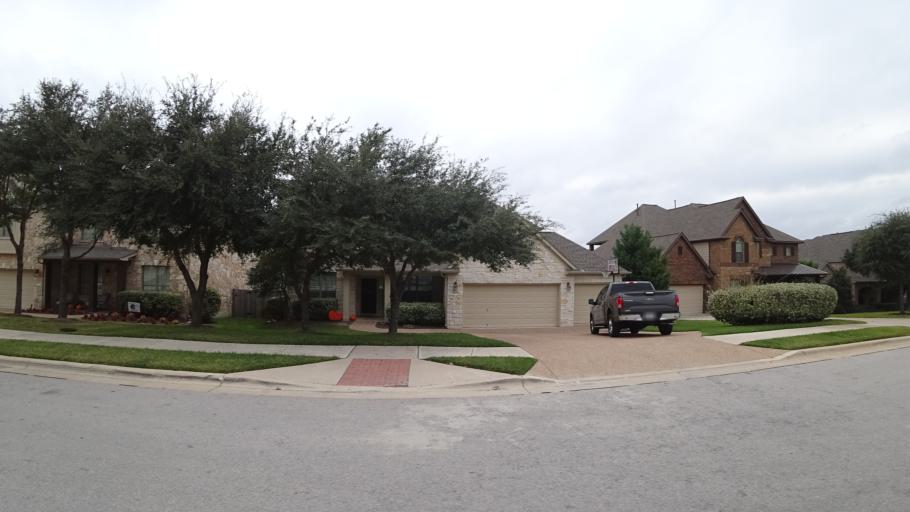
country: US
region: Texas
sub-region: Travis County
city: Hudson Bend
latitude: 30.3590
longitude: -97.9085
